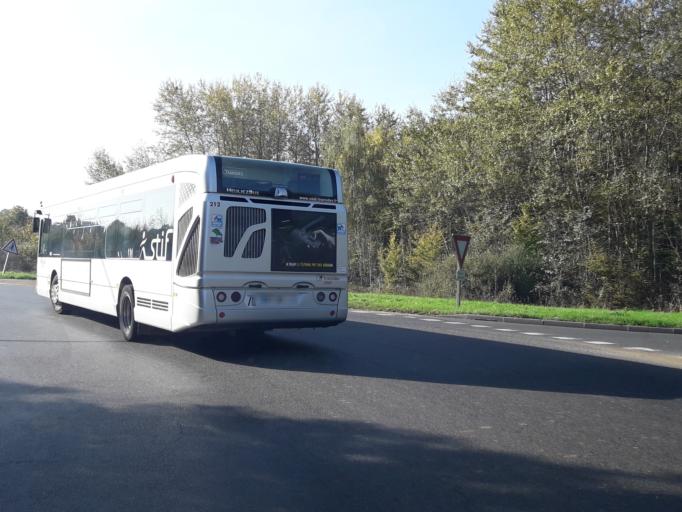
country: FR
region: Ile-de-France
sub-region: Departement de l'Essonne
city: Fleury-Merogis
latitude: 48.6351
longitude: 2.3588
